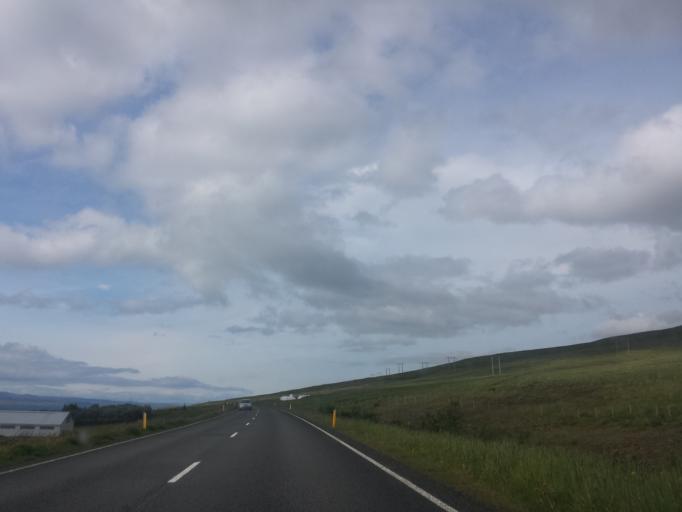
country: IS
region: West
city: Borgarnes
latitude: 65.1995
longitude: -21.0596
